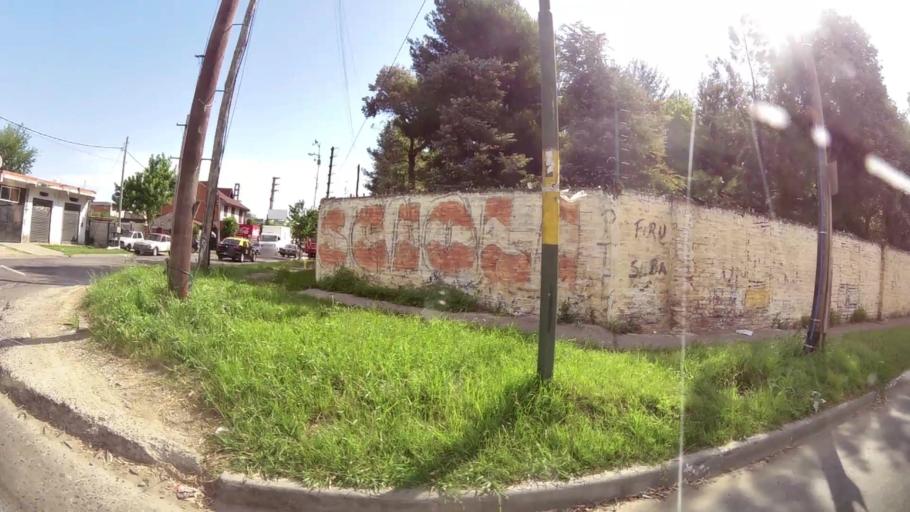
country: AR
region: Buenos Aires
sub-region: Partido de Merlo
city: Merlo
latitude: -34.6376
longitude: -58.7132
